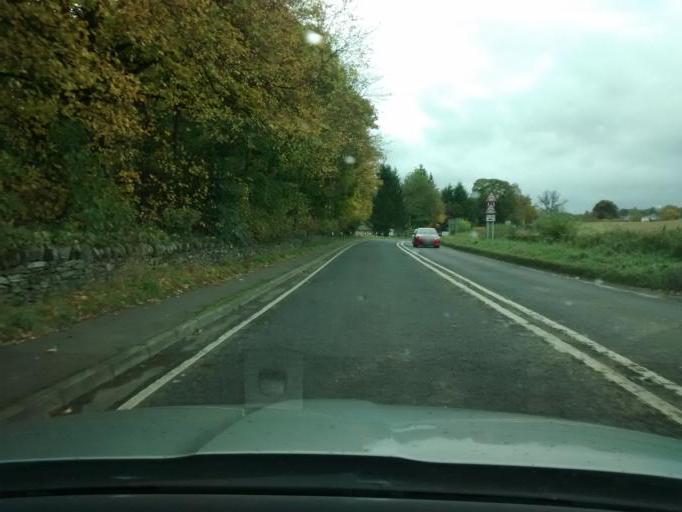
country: GB
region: Scotland
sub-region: Perth and Kinross
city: Auchterarder
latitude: 56.3059
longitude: -3.6761
